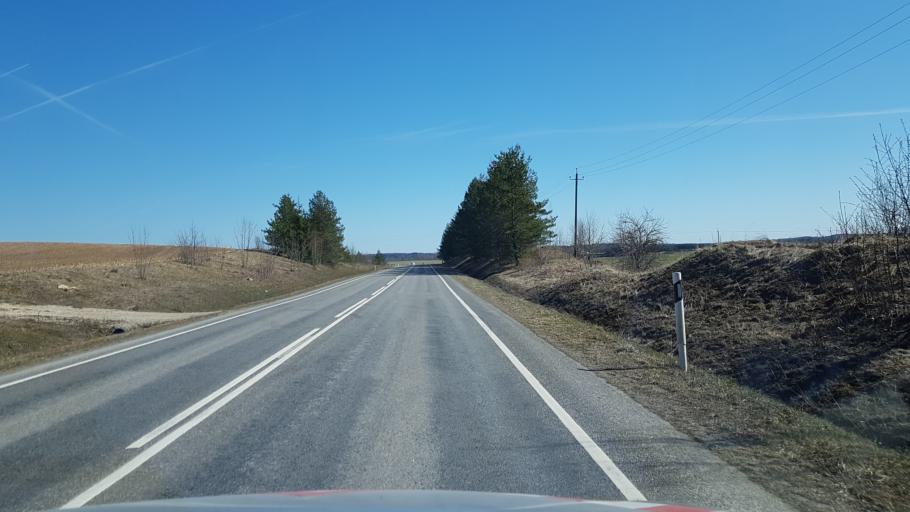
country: EE
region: Laeaene-Virumaa
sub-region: Vinni vald
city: Vinni
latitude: 59.3270
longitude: 26.4199
